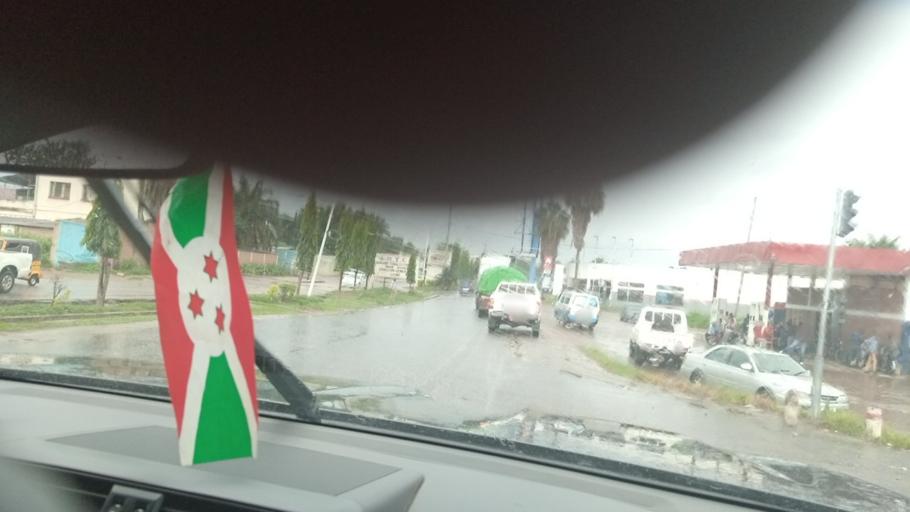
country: BI
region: Bujumbura Mairie
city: Bujumbura
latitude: -3.3742
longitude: 29.3500
